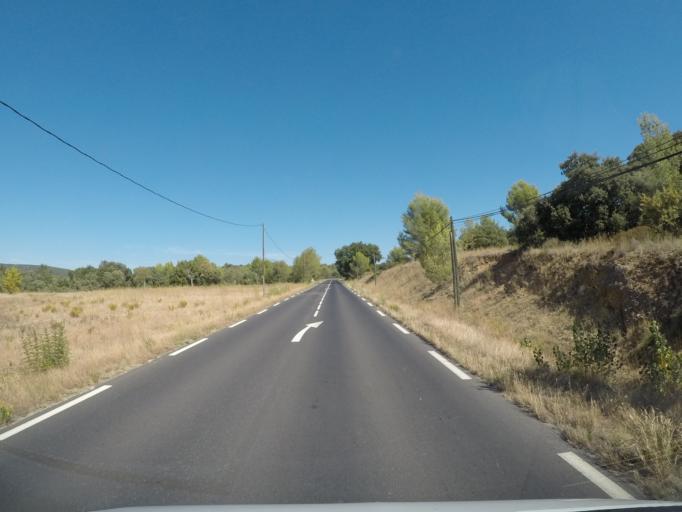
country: FR
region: Languedoc-Roussillon
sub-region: Departement de l'Herault
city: Aniane
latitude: 43.7011
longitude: 3.5932
